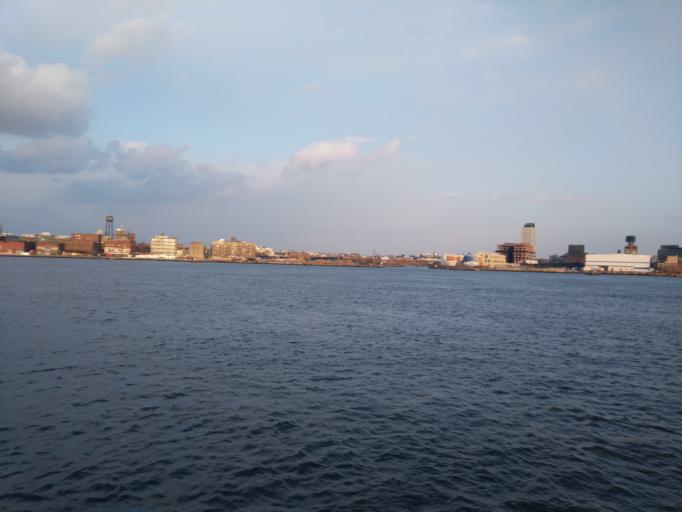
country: US
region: New York
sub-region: Queens County
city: Long Island City
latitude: 40.7271
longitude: -73.9675
